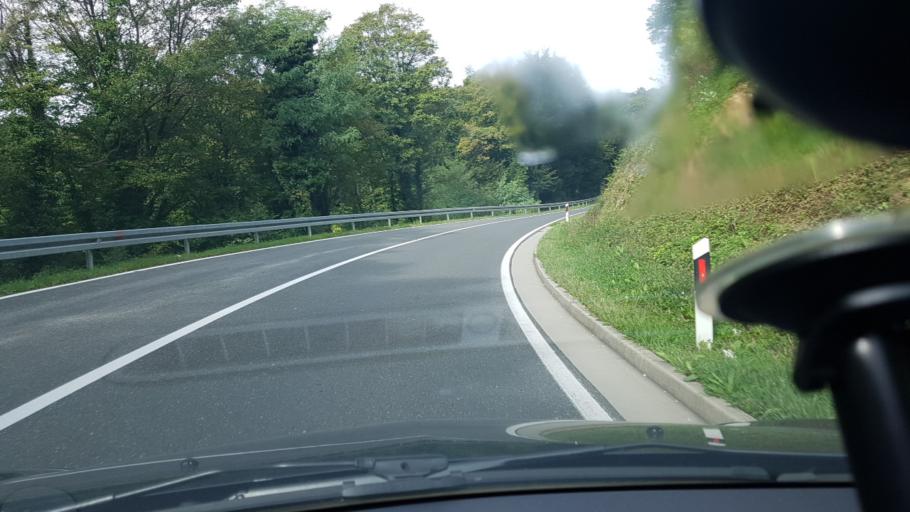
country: HR
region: Varazdinska
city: Ljubescica
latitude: 46.1146
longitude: 16.3560
